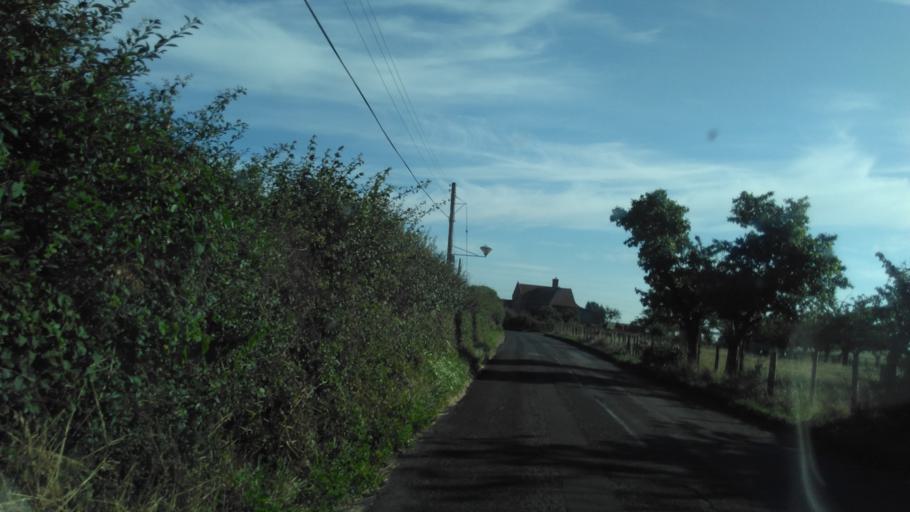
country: GB
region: England
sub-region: Kent
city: Dunkirk
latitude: 51.3288
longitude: 0.9474
